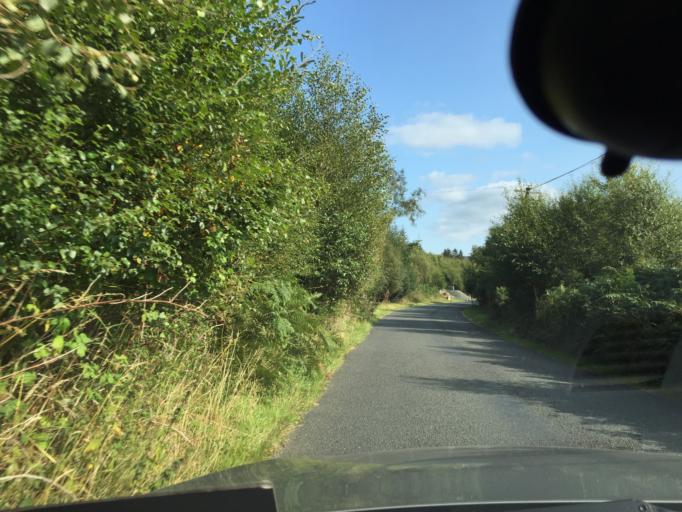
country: IE
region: Leinster
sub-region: Wicklow
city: Rathdrum
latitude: 53.0358
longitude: -6.3209
